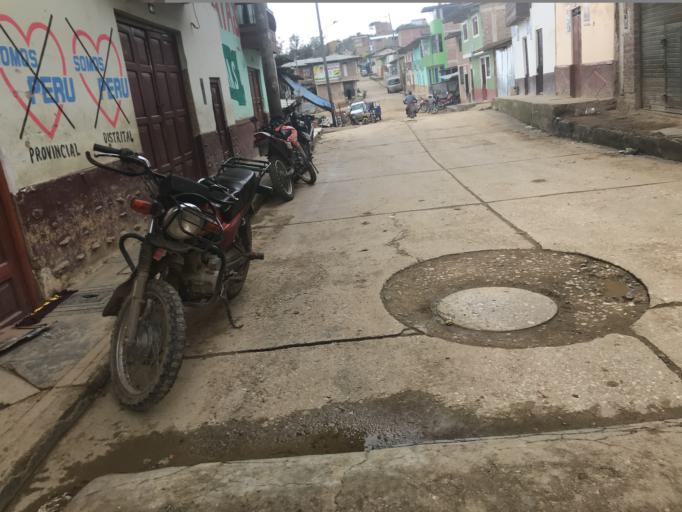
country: PE
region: Cajamarca
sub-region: Provincia de Chota
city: Querocoto
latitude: -6.3600
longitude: -79.0339
